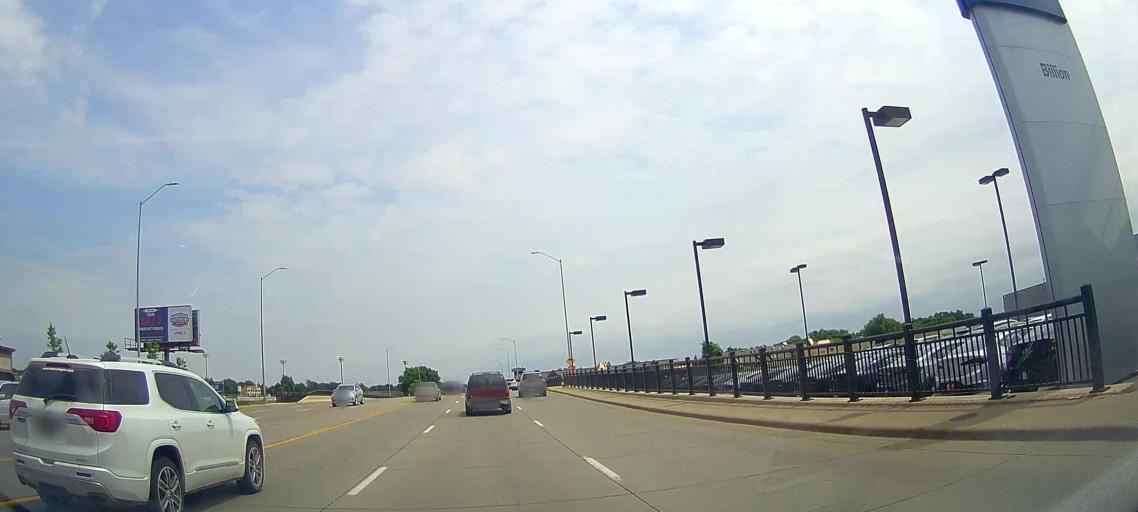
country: US
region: South Dakota
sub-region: Minnehaha County
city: Sioux Falls
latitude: 43.5148
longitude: -96.7678
